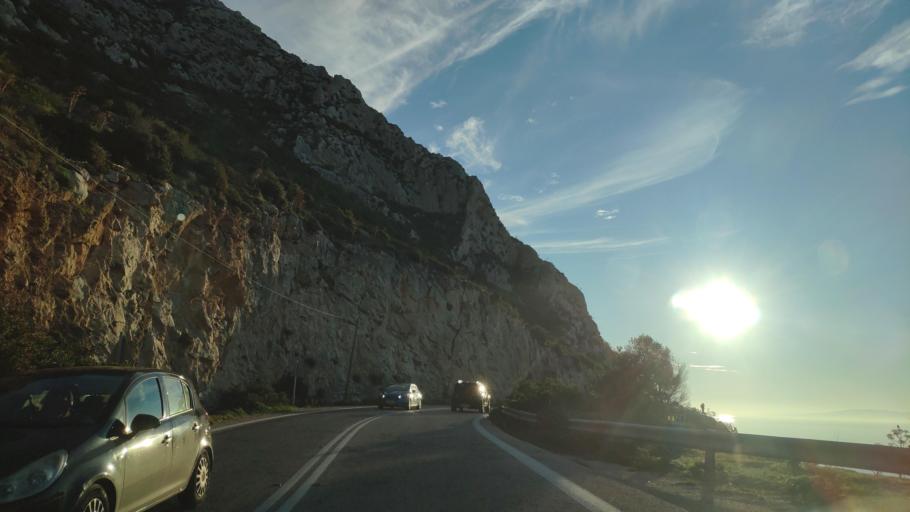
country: GR
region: Attica
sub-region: Nomarchia Anatolikis Attikis
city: Palaia Fokaia
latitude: 37.6765
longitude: 23.9420
